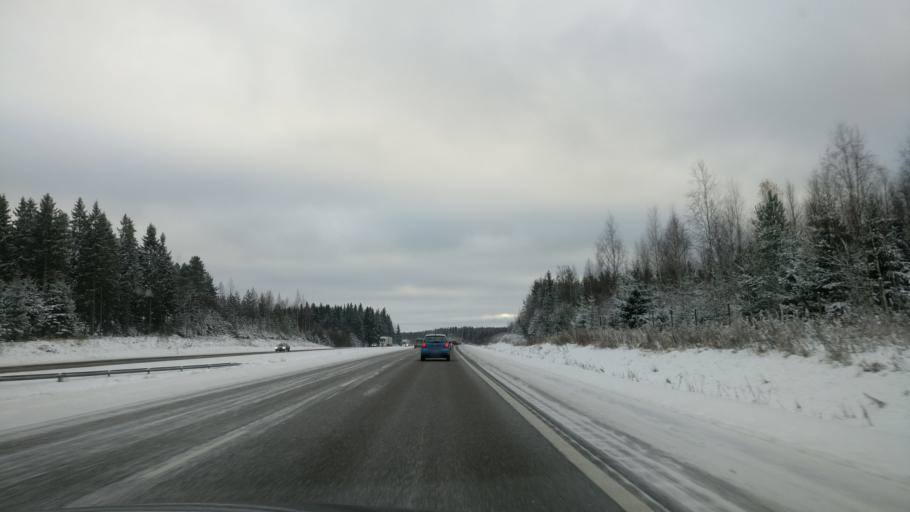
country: FI
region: Paijanne Tavastia
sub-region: Lahti
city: Nastola
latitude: 61.0334
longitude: 25.8418
